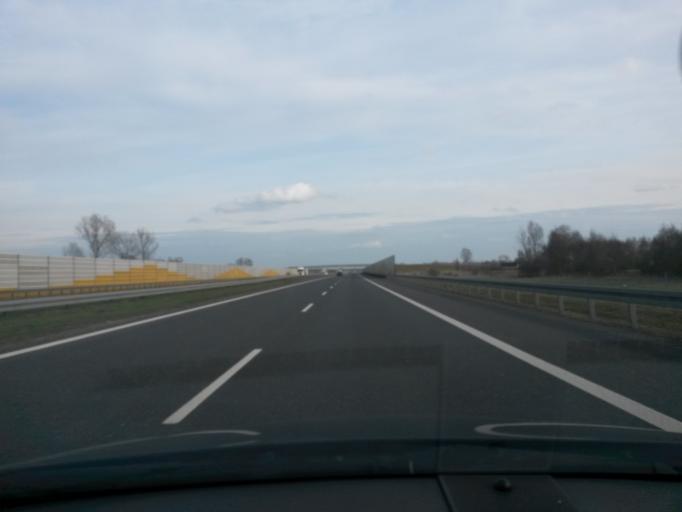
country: PL
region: Greater Poland Voivodeship
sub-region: Powiat kolski
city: Dabie
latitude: 52.0620
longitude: 18.8311
